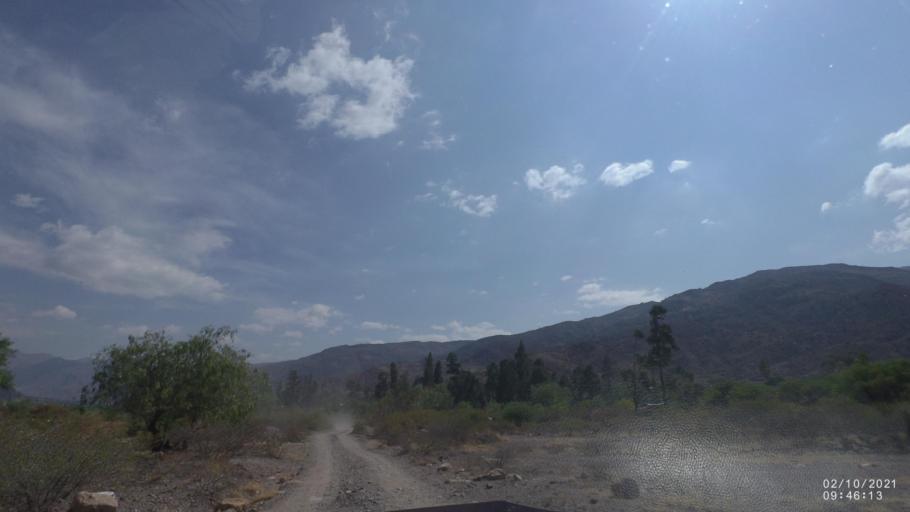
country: BO
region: Cochabamba
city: Irpa Irpa
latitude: -17.8062
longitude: -66.3345
